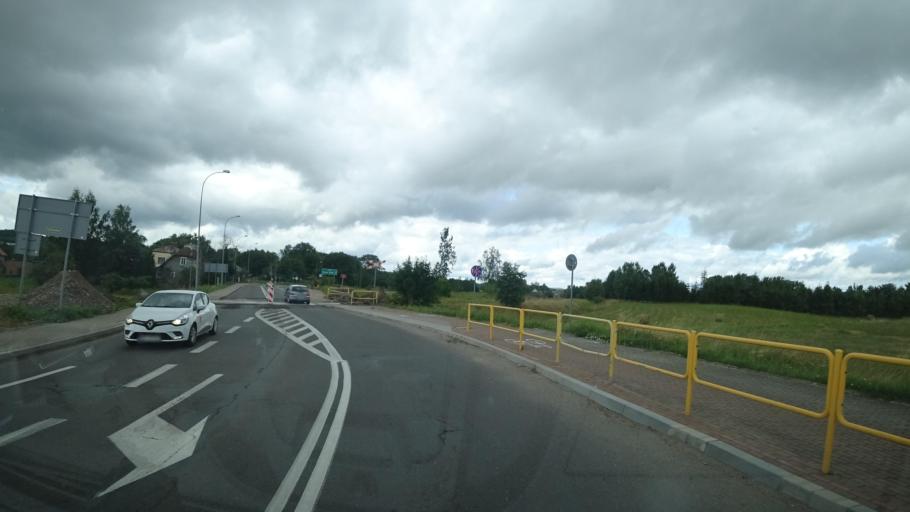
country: PL
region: Warmian-Masurian Voivodeship
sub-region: Powiat olecki
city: Kowale Oleckie
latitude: 54.1748
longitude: 22.4155
